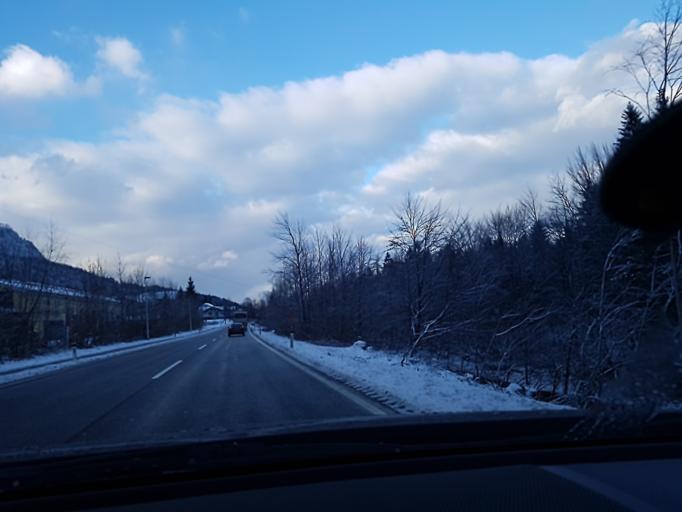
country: AT
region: Salzburg
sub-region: Politischer Bezirk Salzburg-Umgebung
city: Grodig
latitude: 47.7192
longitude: 13.0433
